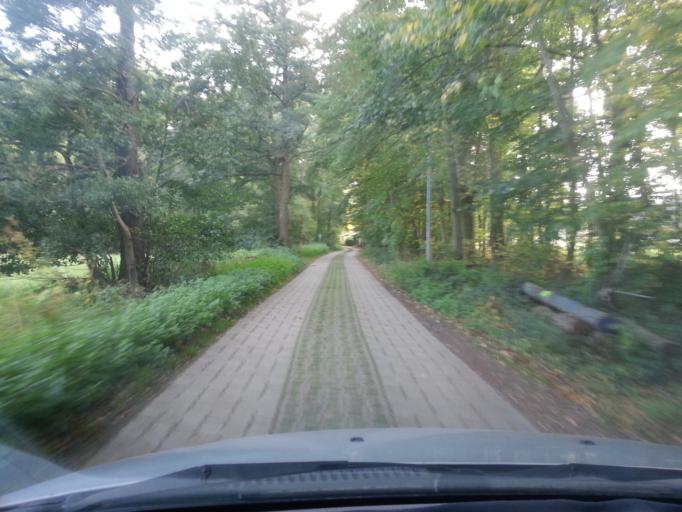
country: DE
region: Rheinland-Pfalz
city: Hassloch
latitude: 49.3455
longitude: 8.2597
